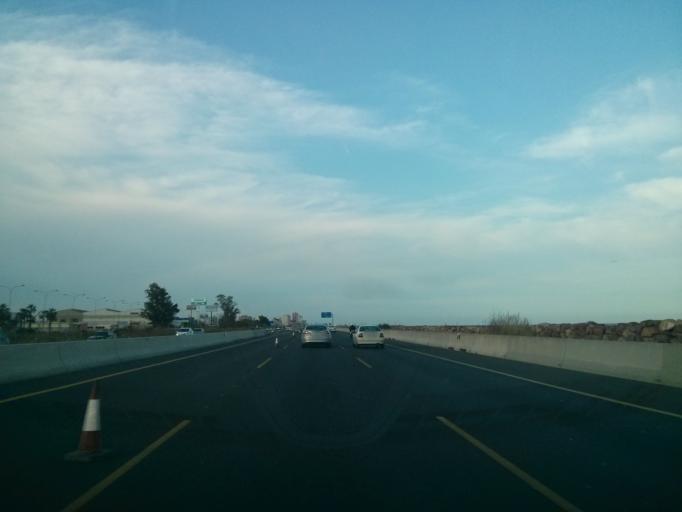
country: ES
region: Valencia
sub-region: Provincia de Valencia
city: Albuixech
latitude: 39.5415
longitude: -0.3031
